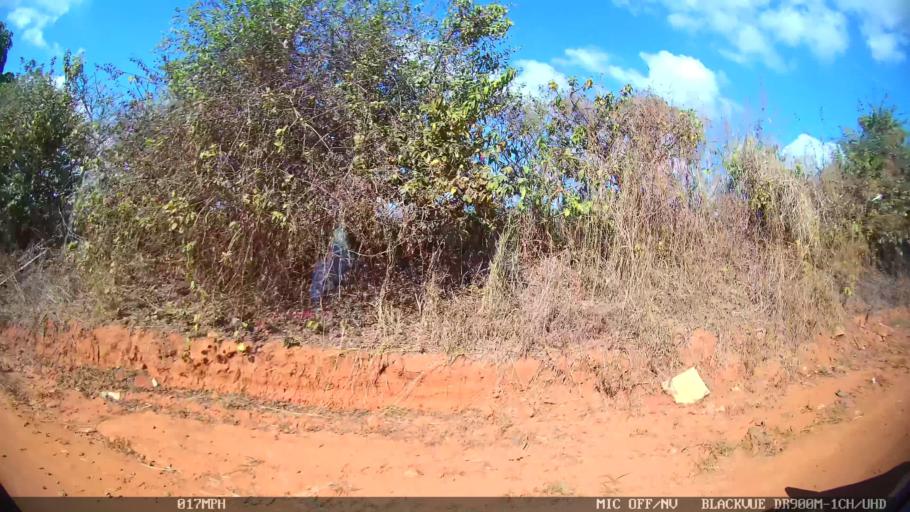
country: BR
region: Sao Paulo
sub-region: Hortolandia
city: Hortolandia
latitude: -22.8788
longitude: -47.2645
